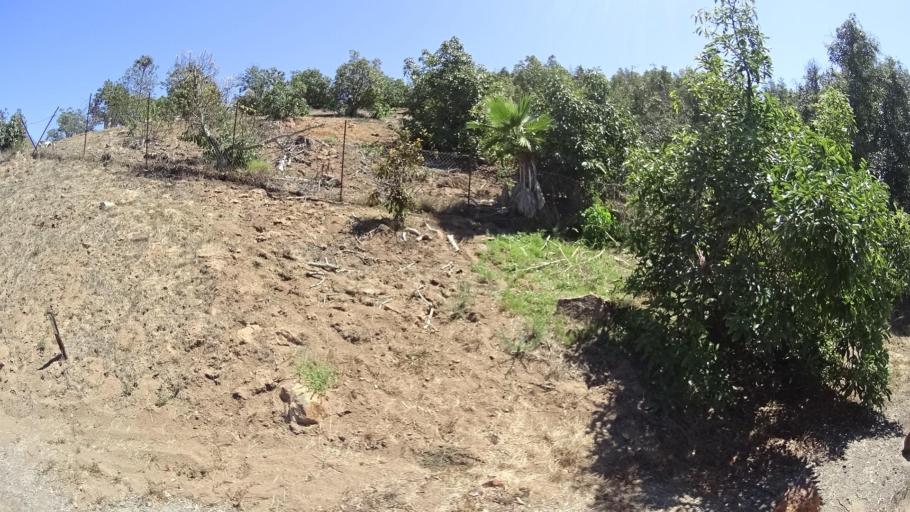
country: US
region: California
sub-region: San Diego County
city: Rainbow
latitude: 33.3498
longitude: -117.1798
